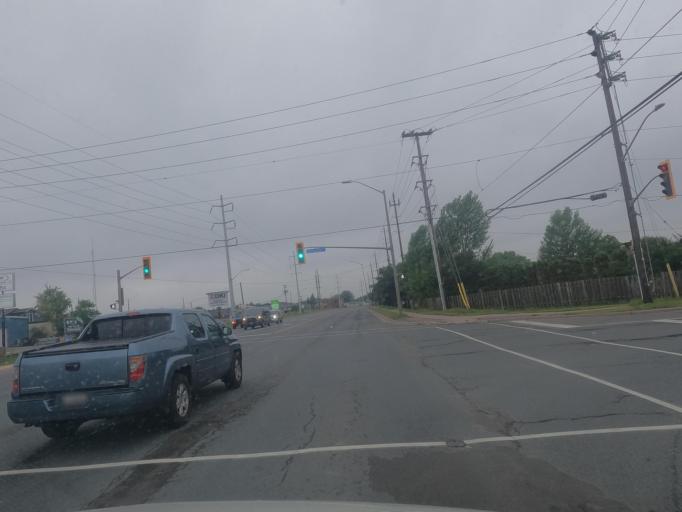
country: CA
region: Ontario
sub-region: Algoma
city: Sault Ste. Marie
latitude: 46.5383
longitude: -84.3294
